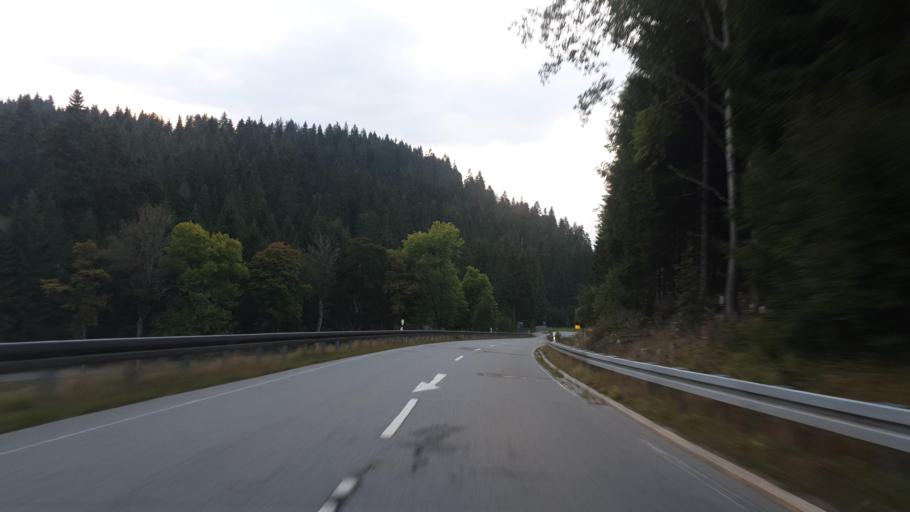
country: DE
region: Saxony
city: Johanngeorgenstadt
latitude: 50.4326
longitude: 12.6472
